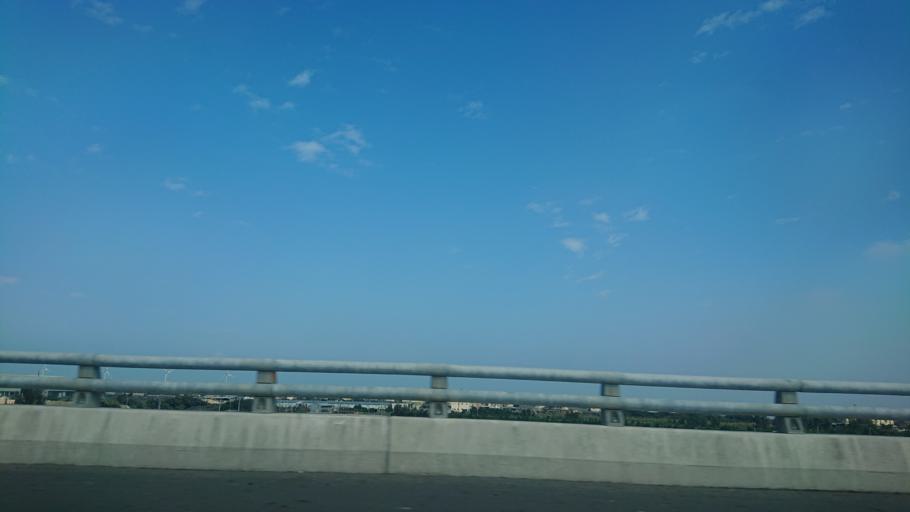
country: TW
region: Taiwan
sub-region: Changhua
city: Chang-hua
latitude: 23.9708
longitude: 120.3484
